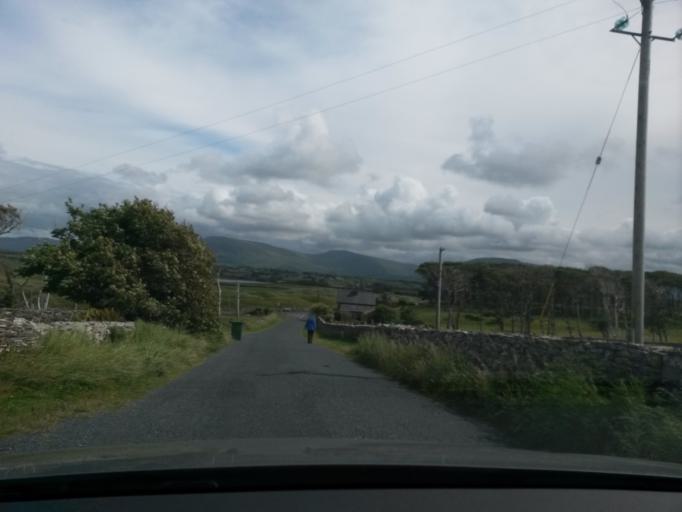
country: IE
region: Connaught
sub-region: County Leitrim
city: Kinlough
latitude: 54.4587
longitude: -8.4575
